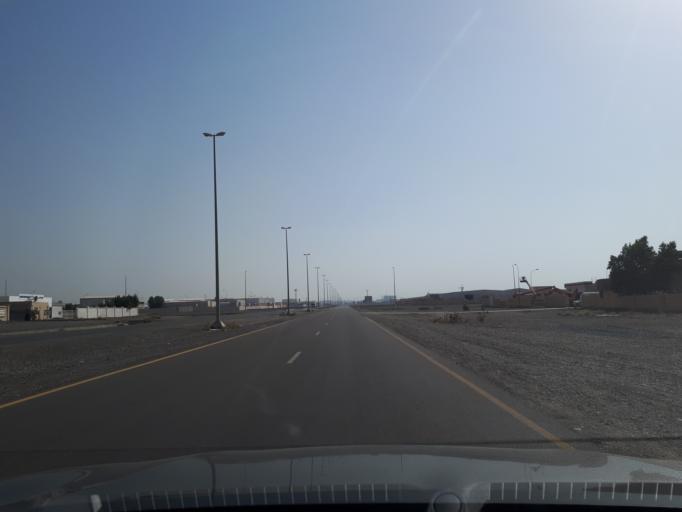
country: OM
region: Al Batinah
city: Al Liwa'
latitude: 24.4387
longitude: 56.5830
